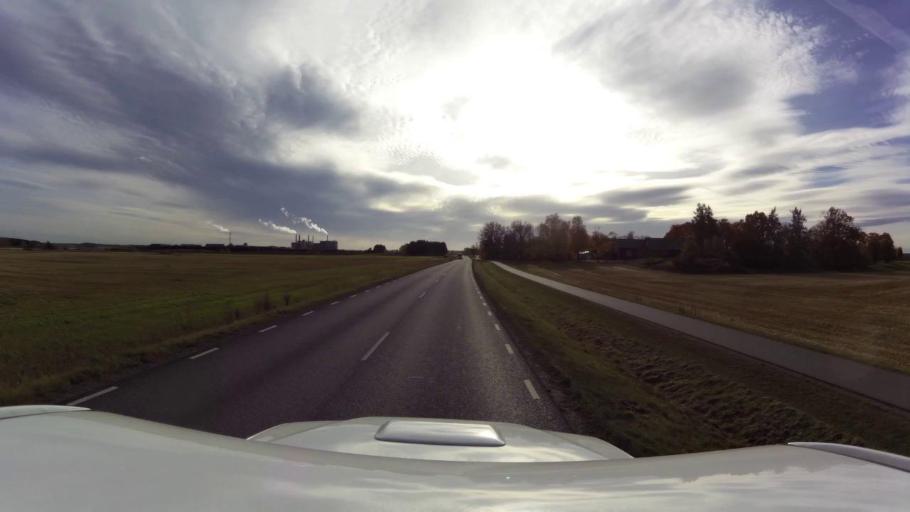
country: SE
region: OEstergoetland
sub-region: Linkopings Kommun
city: Ekangen
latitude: 58.4477
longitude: 15.6453
